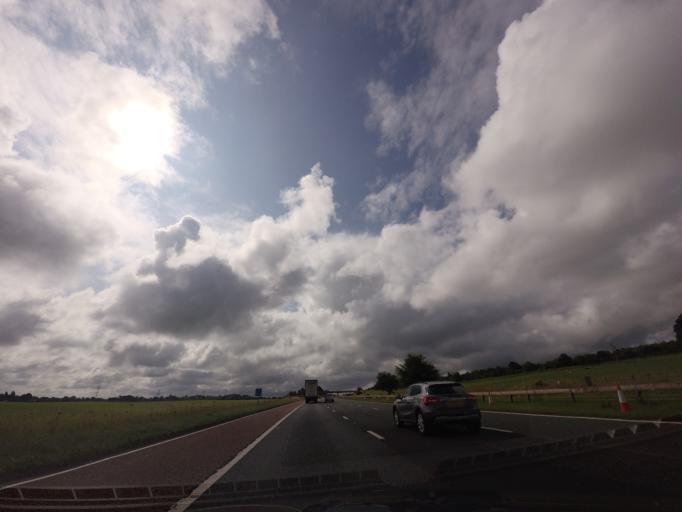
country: GB
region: England
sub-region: Cumbria
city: Penrith
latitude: 54.6012
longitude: -2.7046
